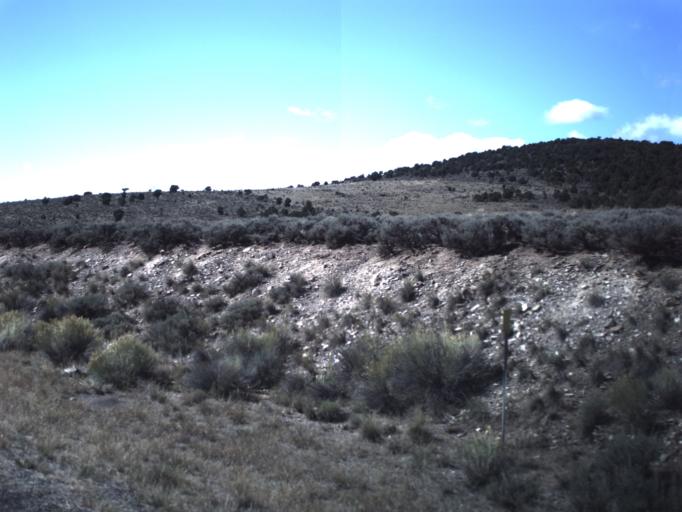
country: US
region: Utah
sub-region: Sevier County
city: Monroe
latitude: 38.5469
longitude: -111.8702
